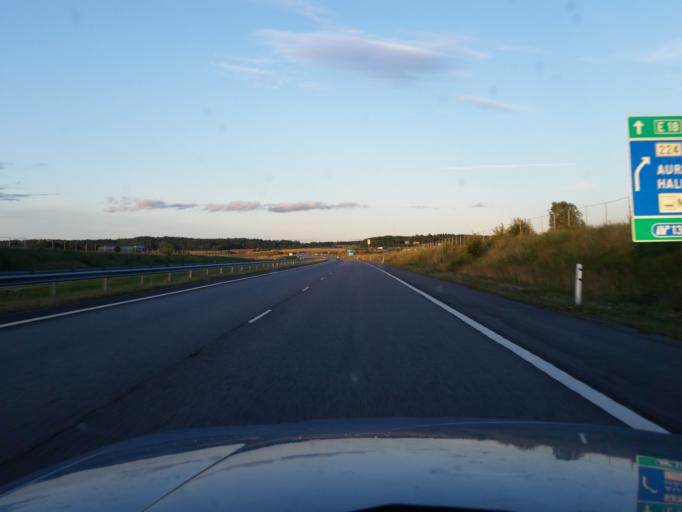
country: FI
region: Varsinais-Suomi
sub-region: Salo
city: Halikko
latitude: 60.4289
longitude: 23.0158
